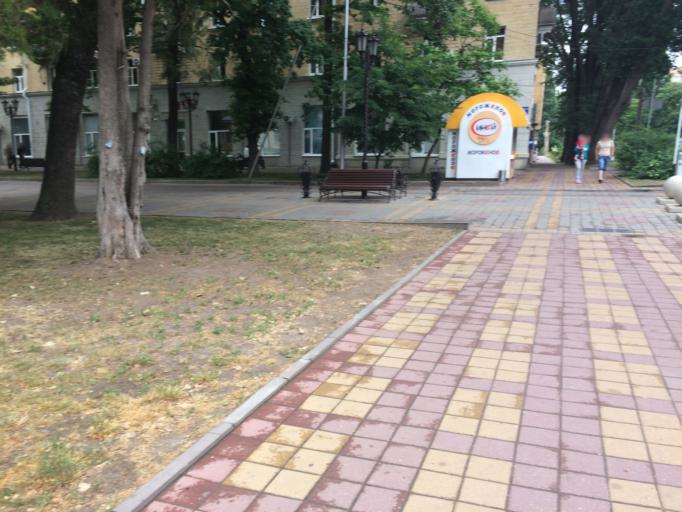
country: RU
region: Stavropol'skiy
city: Stavropol'
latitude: 45.0400
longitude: 41.9732
